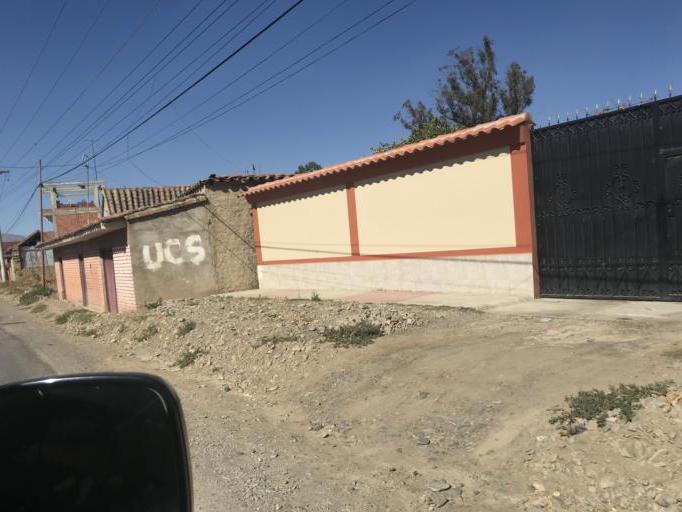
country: BO
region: Cochabamba
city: Cliza
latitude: -17.5650
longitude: -65.8871
